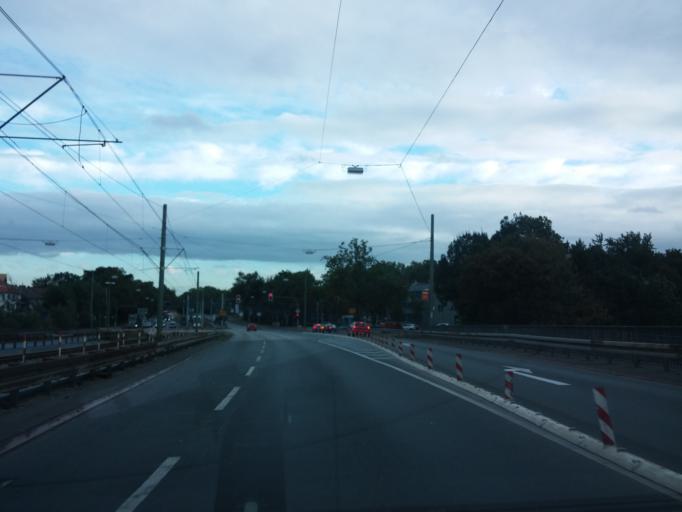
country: DE
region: North Rhine-Westphalia
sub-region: Regierungsbezirk Munster
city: Gelsenkirchen
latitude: 51.5376
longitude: 7.0708
